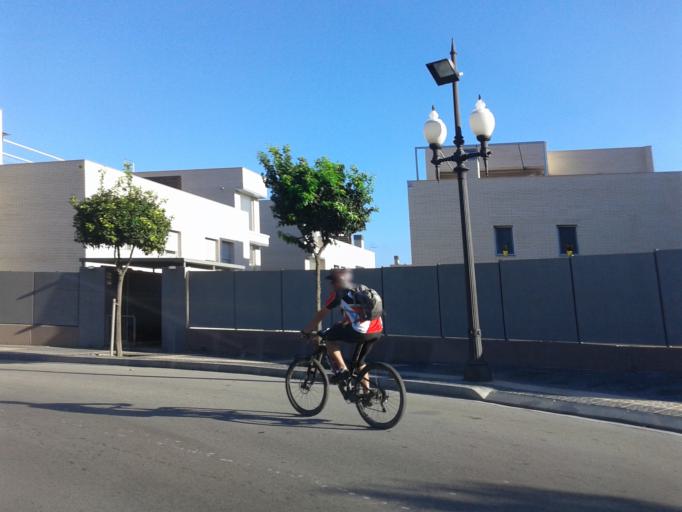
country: ES
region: Catalonia
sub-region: Provincia de Tarragona
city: Tarragona
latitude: 41.1217
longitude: 1.2756
